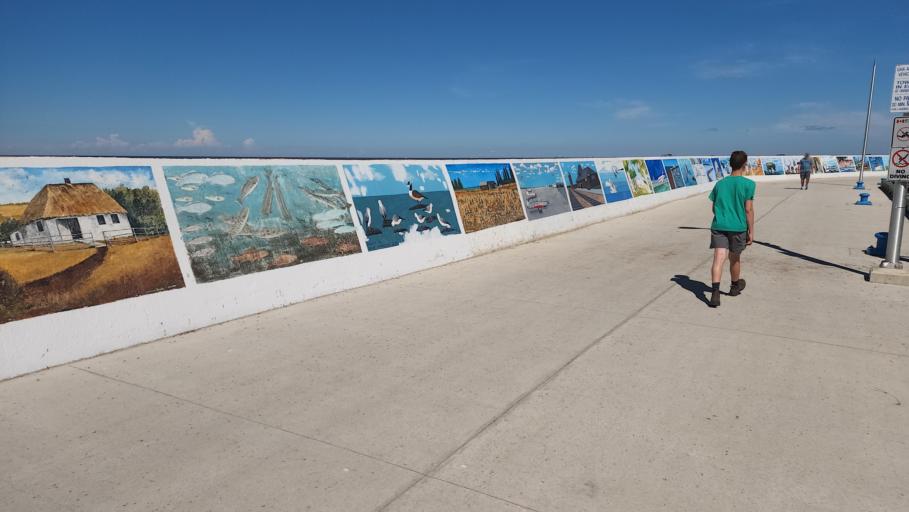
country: CA
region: Manitoba
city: Gimli
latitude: 50.6320
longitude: -96.9838
